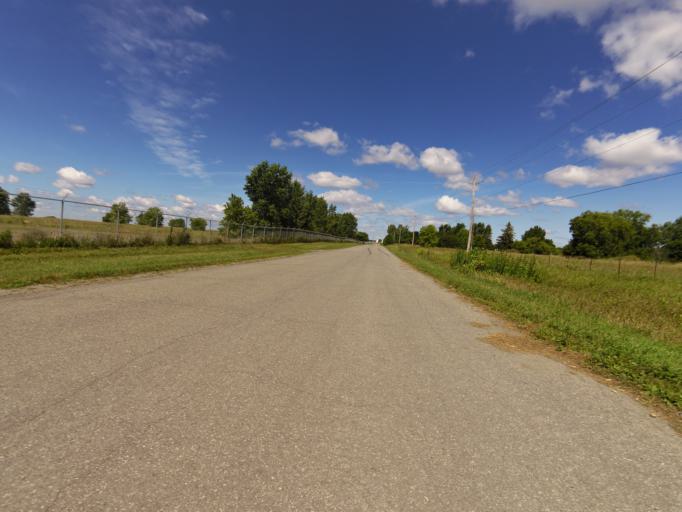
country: CA
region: Ontario
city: Ottawa
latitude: 45.3109
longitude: -75.6478
